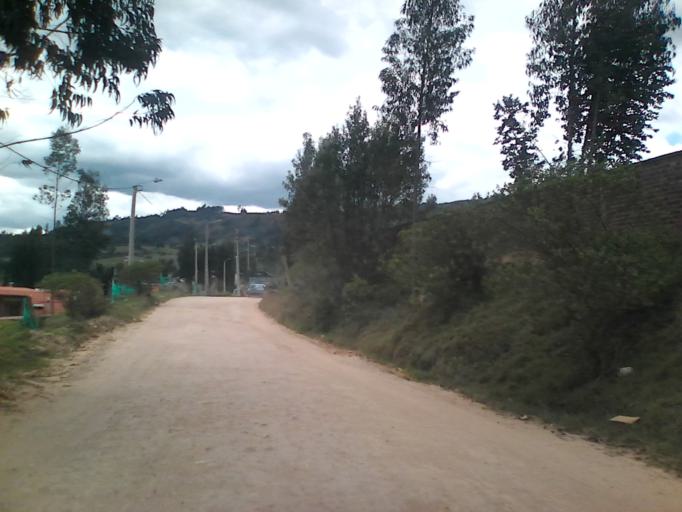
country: CO
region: Boyaca
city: Duitama
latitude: 5.8279
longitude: -73.0738
